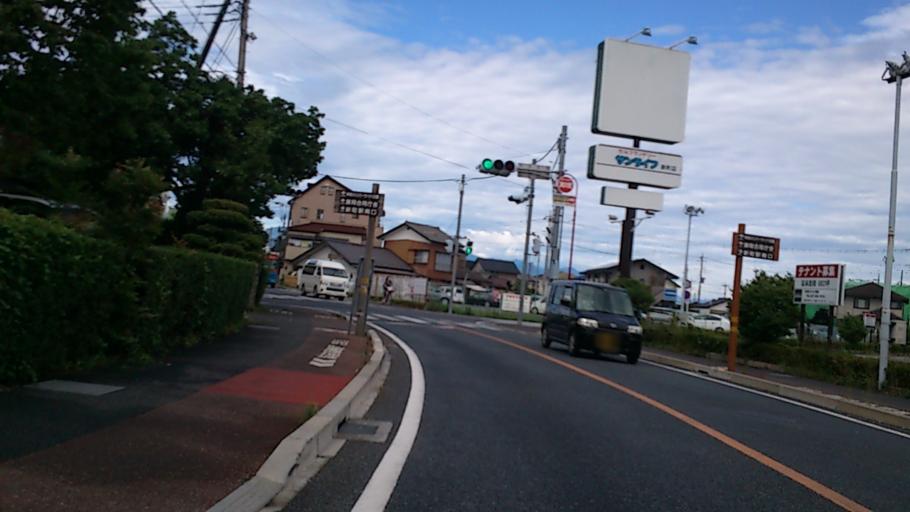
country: JP
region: Gunma
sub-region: Sawa-gun
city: Tamamura
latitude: 36.2711
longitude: 139.1067
